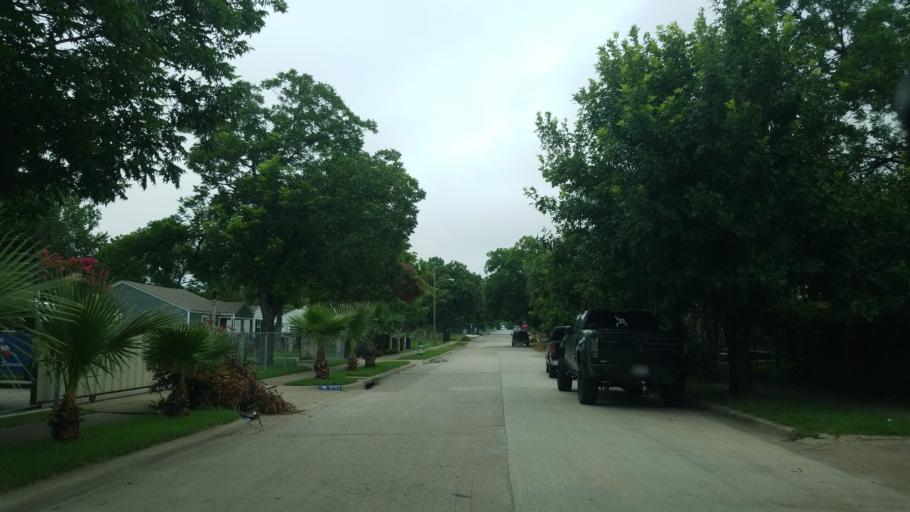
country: US
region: Texas
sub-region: Dallas County
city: University Park
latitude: 32.8365
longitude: -96.8631
